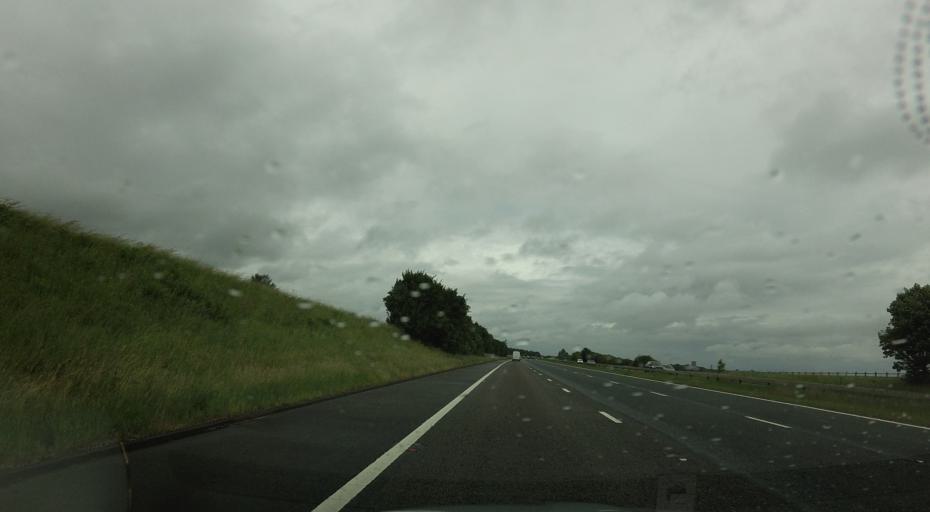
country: GB
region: England
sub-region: Cumbria
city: Scotby
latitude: 54.7740
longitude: -2.8489
